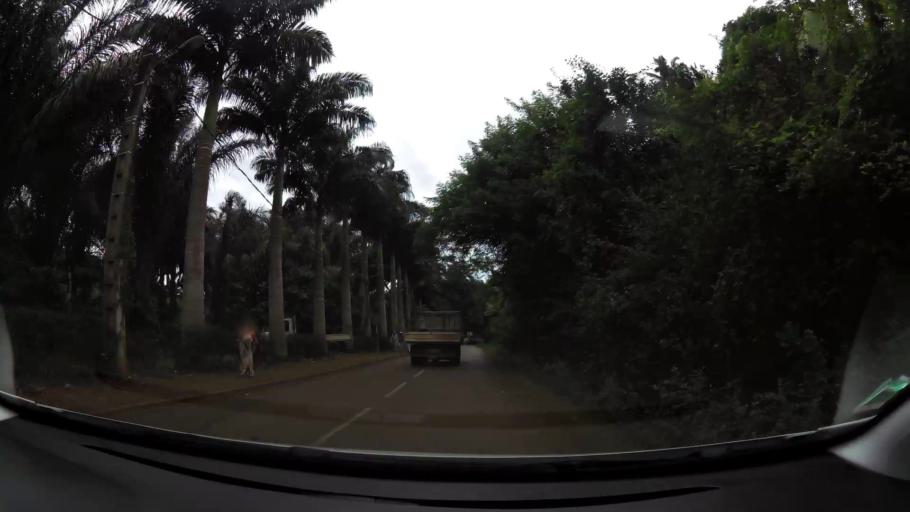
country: YT
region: Chiconi
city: Chiconi
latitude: -12.8327
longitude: 45.1178
